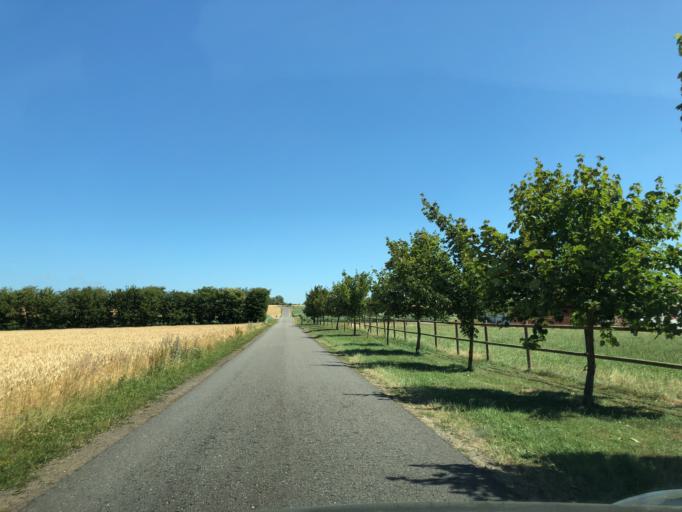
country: DK
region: North Denmark
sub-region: Mariagerfjord Kommune
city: Hobro
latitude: 56.6020
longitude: 9.6808
